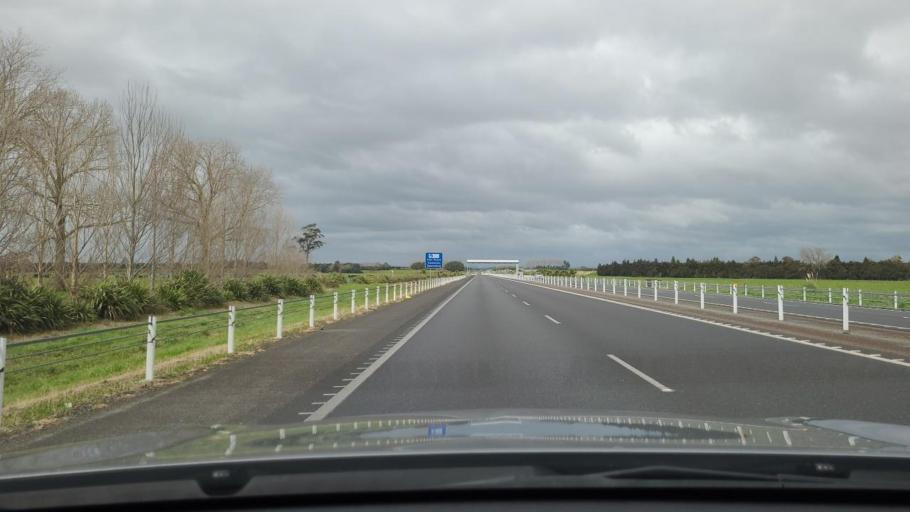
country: NZ
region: Bay of Plenty
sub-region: Western Bay of Plenty District
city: Maketu
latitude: -37.7718
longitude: 176.3785
